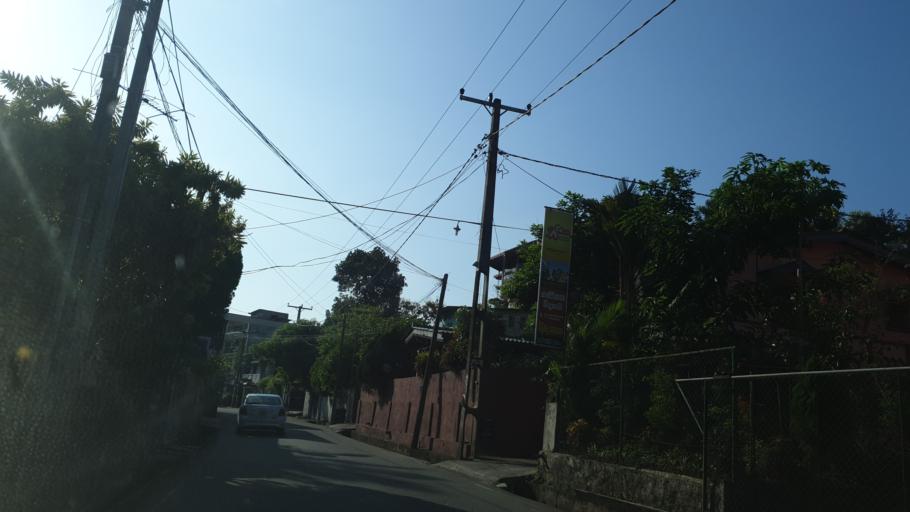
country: LK
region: Western
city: Sri Jayewardenepura Kotte
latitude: 6.8720
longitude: 79.9150
